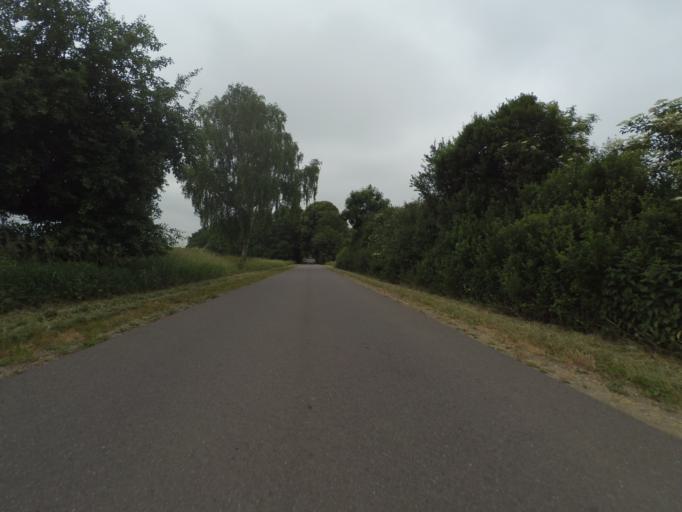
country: DE
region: Mecklenburg-Vorpommern
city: Plau am See
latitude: 53.5117
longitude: 12.1799
